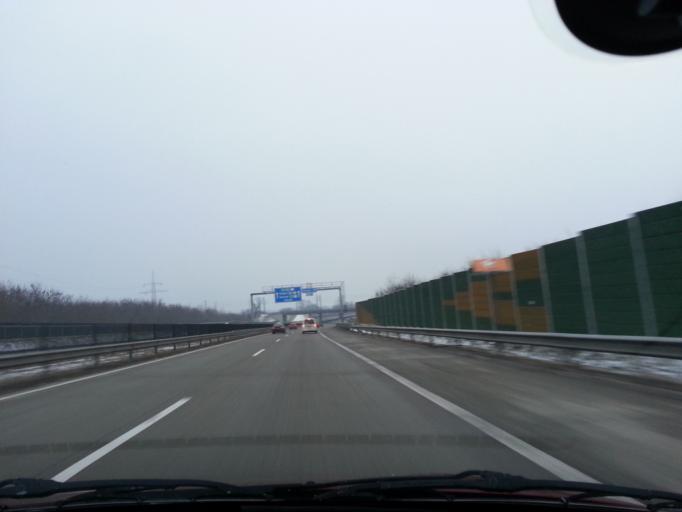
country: HU
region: Pest
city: Ecser
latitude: 47.4449
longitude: 19.3323
